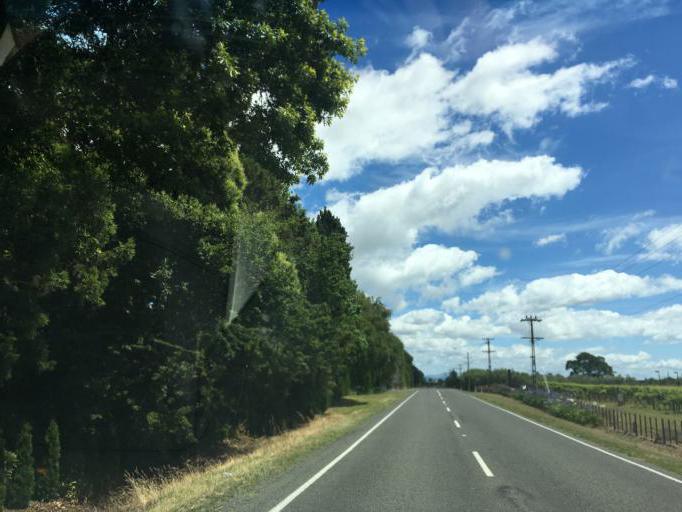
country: NZ
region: Hawke's Bay
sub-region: Hastings District
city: Hastings
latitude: -39.6446
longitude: 176.9090
